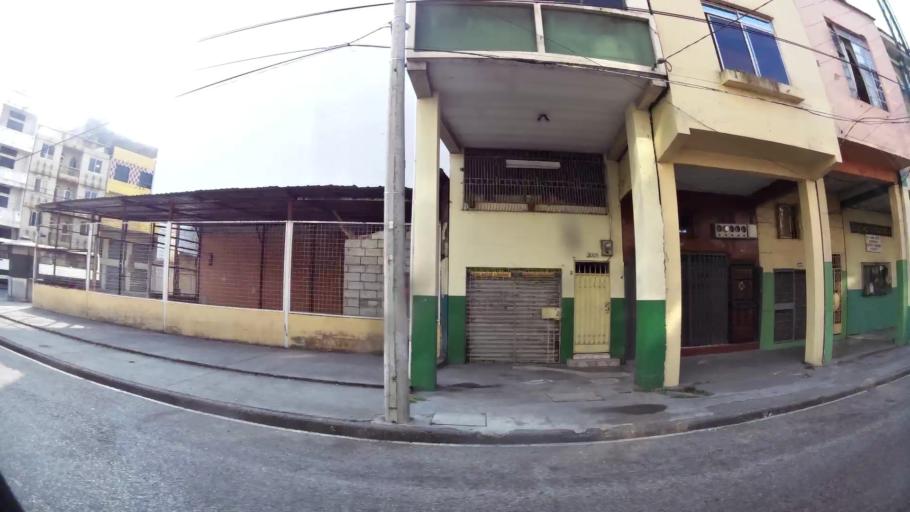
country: EC
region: Guayas
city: Guayaquil
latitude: -2.1988
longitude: -79.8873
